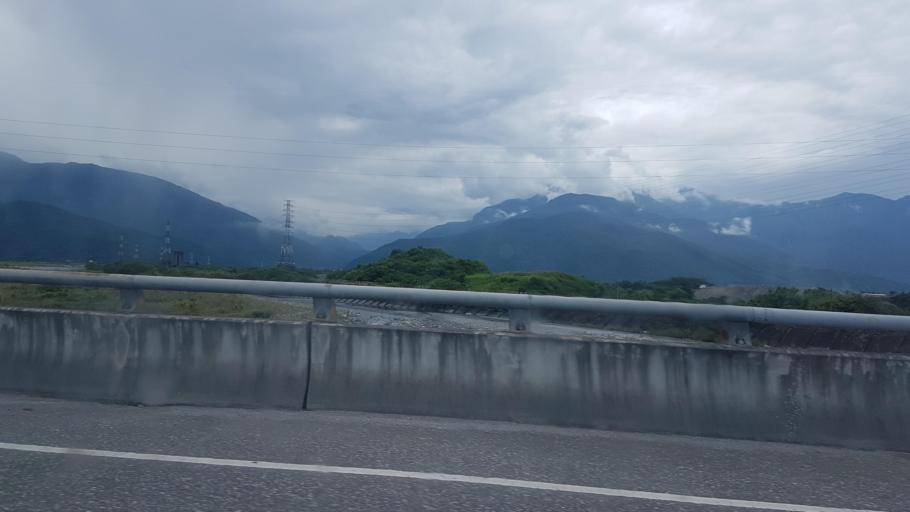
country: TW
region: Taiwan
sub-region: Hualien
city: Hualian
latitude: 23.9189
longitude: 121.5841
